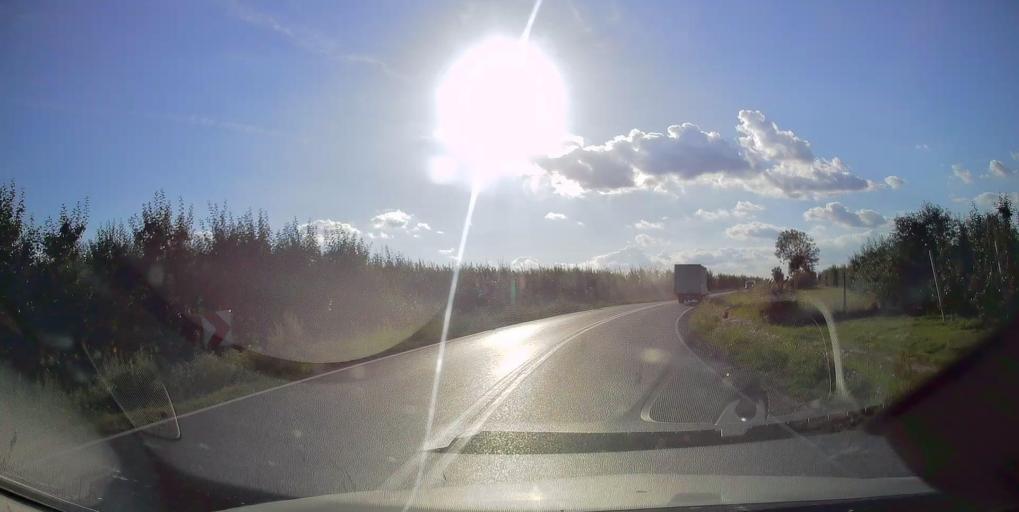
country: PL
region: Masovian Voivodeship
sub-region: Powiat grojecki
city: Bledow
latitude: 51.8061
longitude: 20.6894
